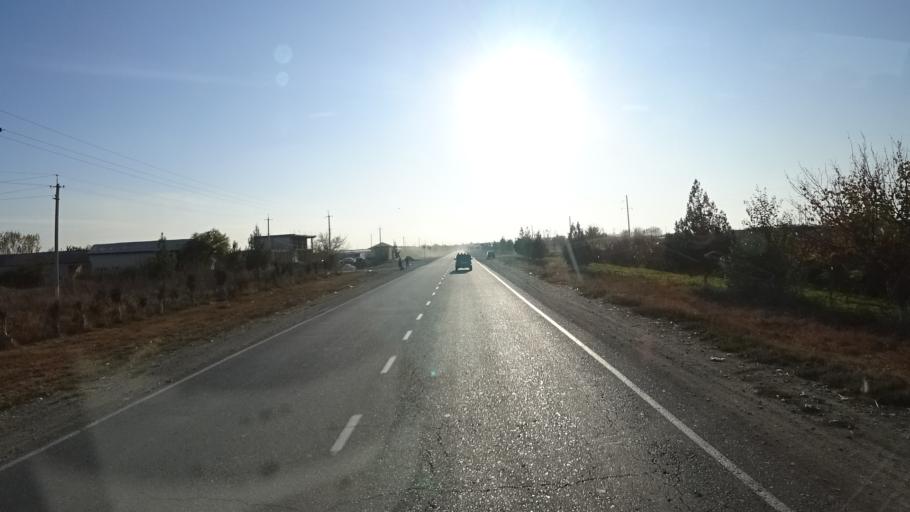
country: UZ
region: Navoiy
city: Beshrabot
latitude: 40.1757
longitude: 65.3442
